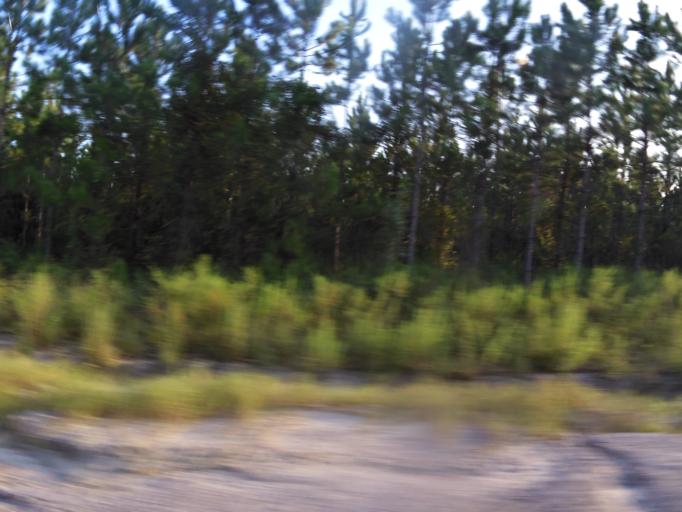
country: US
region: Florida
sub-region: Baker County
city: Macclenny
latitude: 30.3938
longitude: -82.1042
